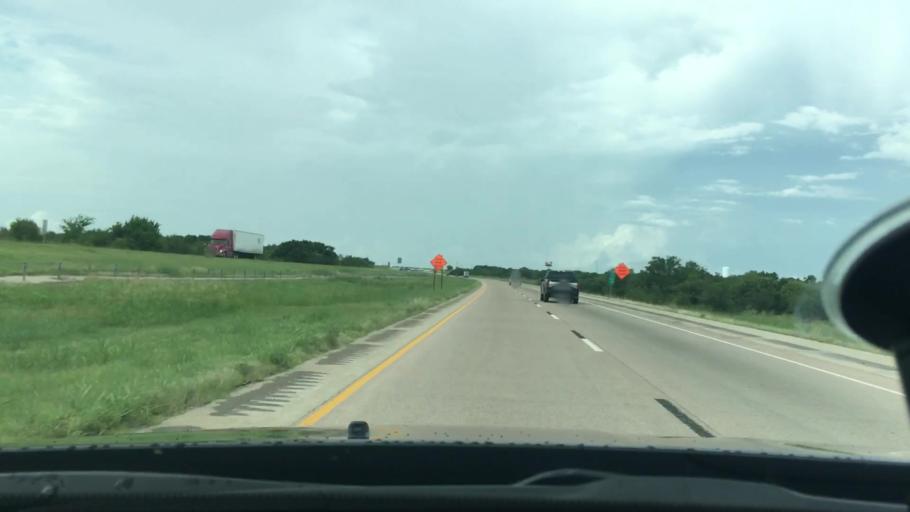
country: US
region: Oklahoma
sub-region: Garvin County
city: Pauls Valley
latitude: 34.6935
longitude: -97.2342
